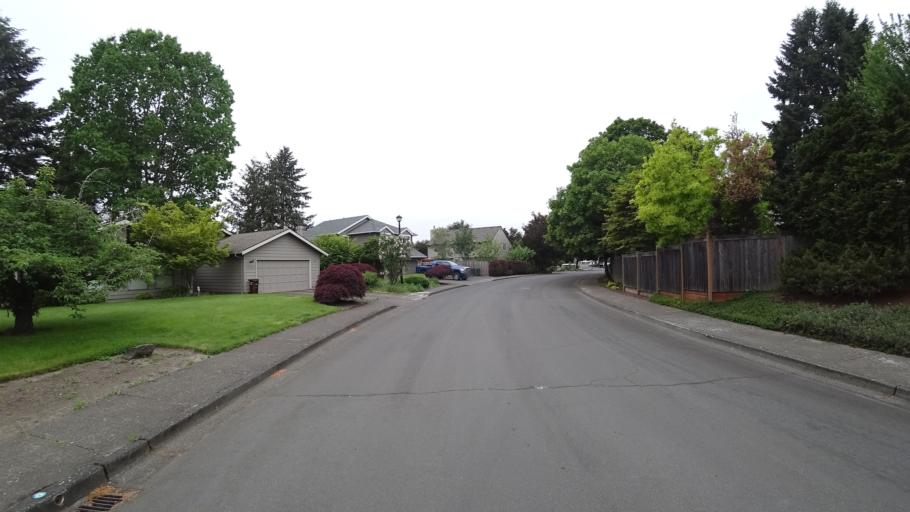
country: US
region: Oregon
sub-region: Washington County
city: Rockcreek
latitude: 45.5627
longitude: -122.8924
